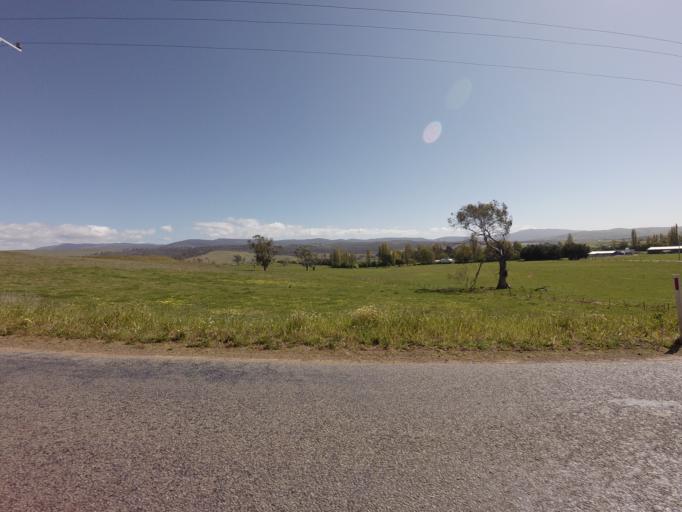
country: AU
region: Tasmania
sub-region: Derwent Valley
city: New Norfolk
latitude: -42.5360
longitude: 146.7530
